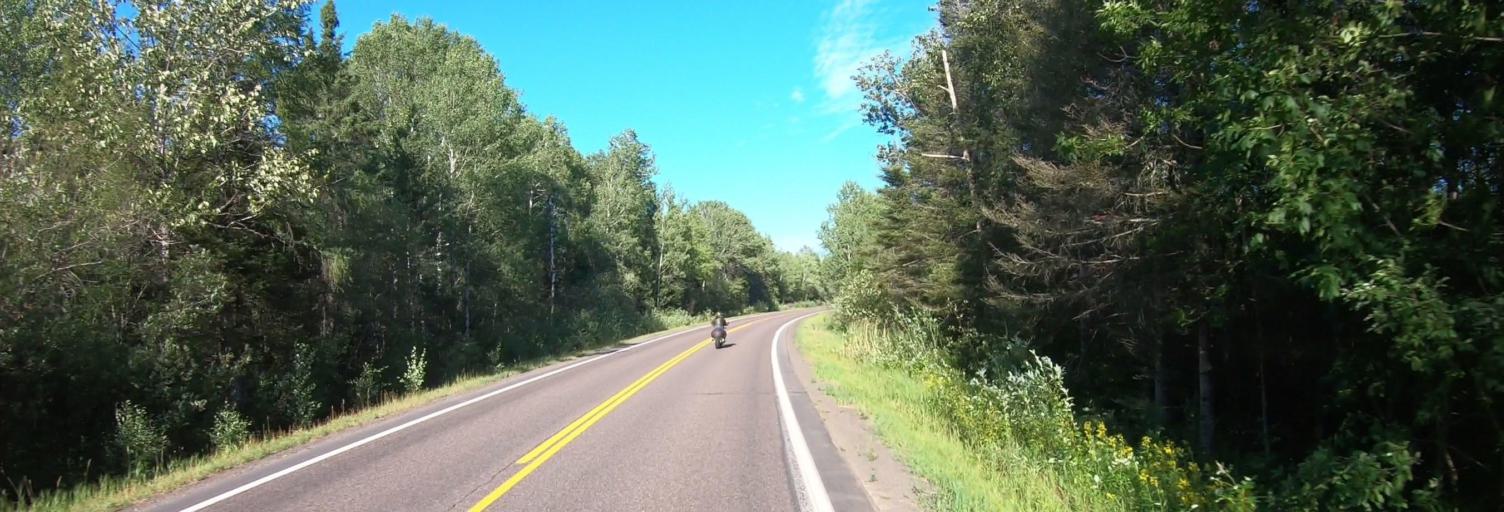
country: US
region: Minnesota
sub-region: Saint Louis County
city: Ely
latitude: 47.9343
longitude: -91.6972
